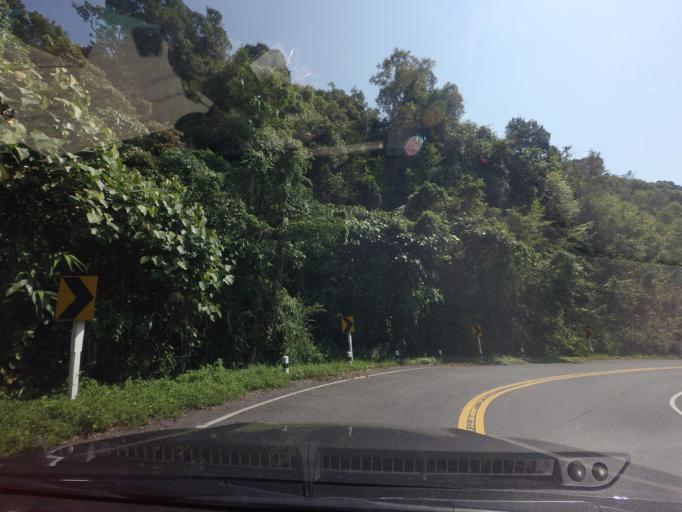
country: TH
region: Nan
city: Bo Kluea
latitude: 19.0400
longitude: 101.0877
